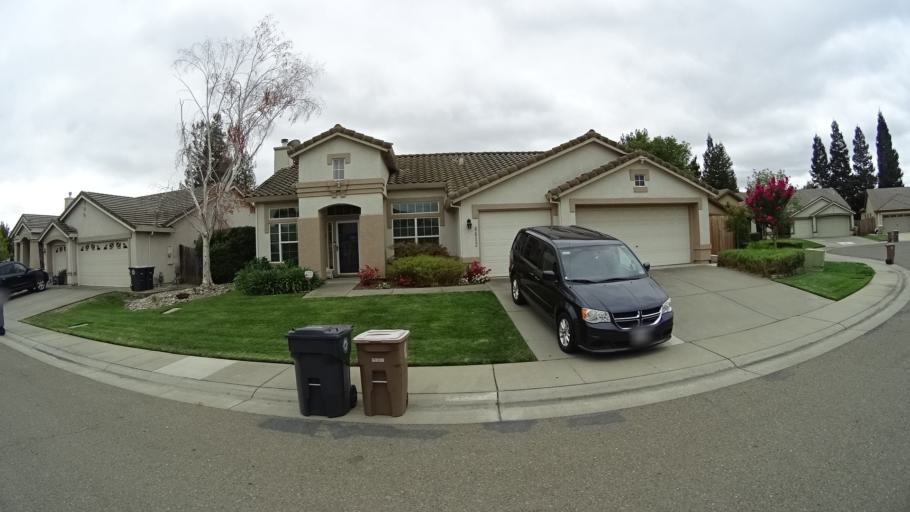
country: US
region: California
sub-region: Sacramento County
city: Laguna
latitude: 38.4174
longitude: -121.4527
